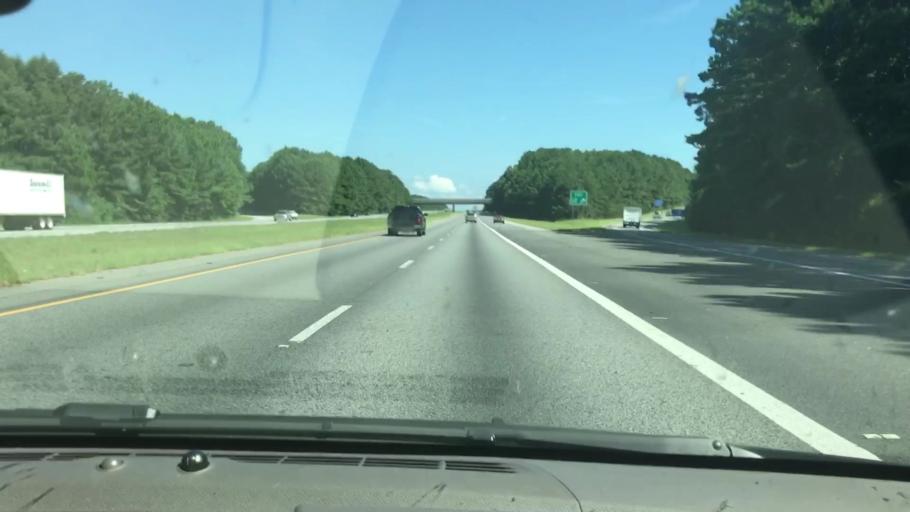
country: US
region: Alabama
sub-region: Russell County
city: Phenix City
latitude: 32.5613
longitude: -84.9623
